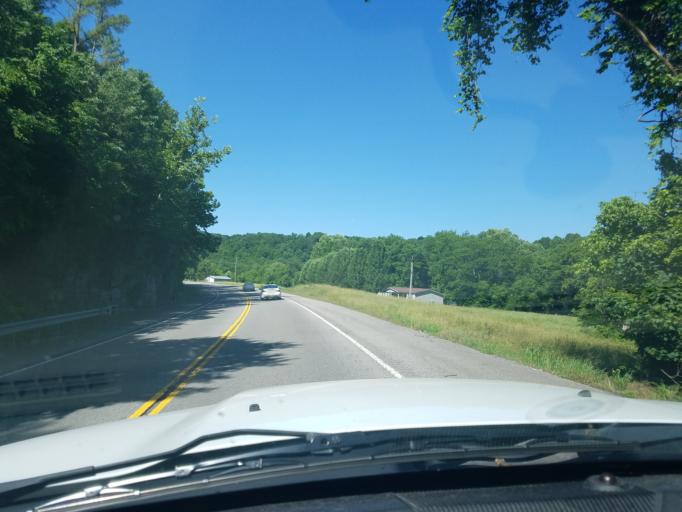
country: US
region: Tennessee
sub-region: Sumner County
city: Westmoreland
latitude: 36.5220
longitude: -86.2598
